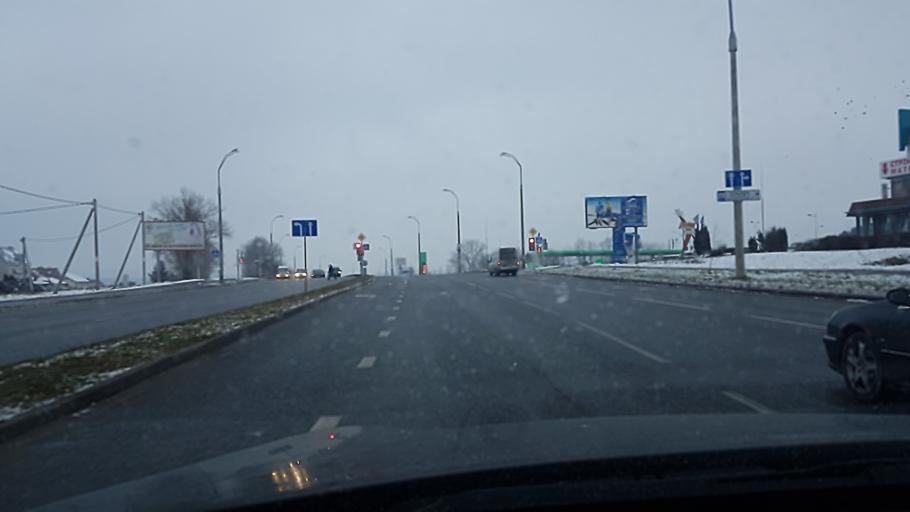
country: BY
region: Minsk
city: Bal'shavik
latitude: 53.9589
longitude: 27.5366
